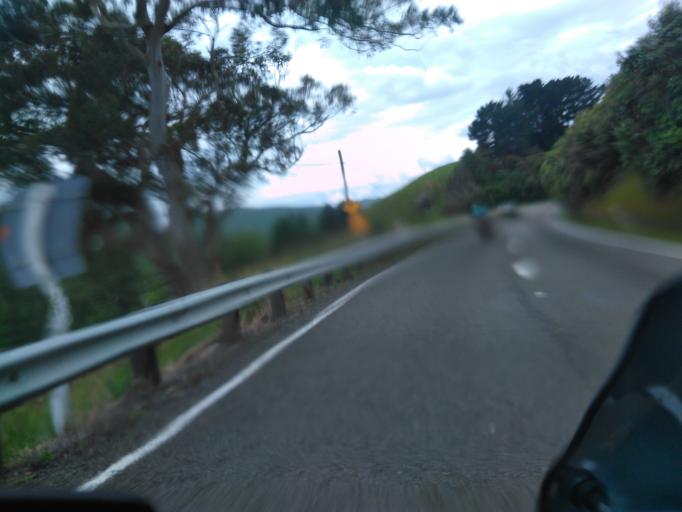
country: NZ
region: Bay of Plenty
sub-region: Opotiki District
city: Opotiki
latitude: -38.3929
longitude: 177.5604
